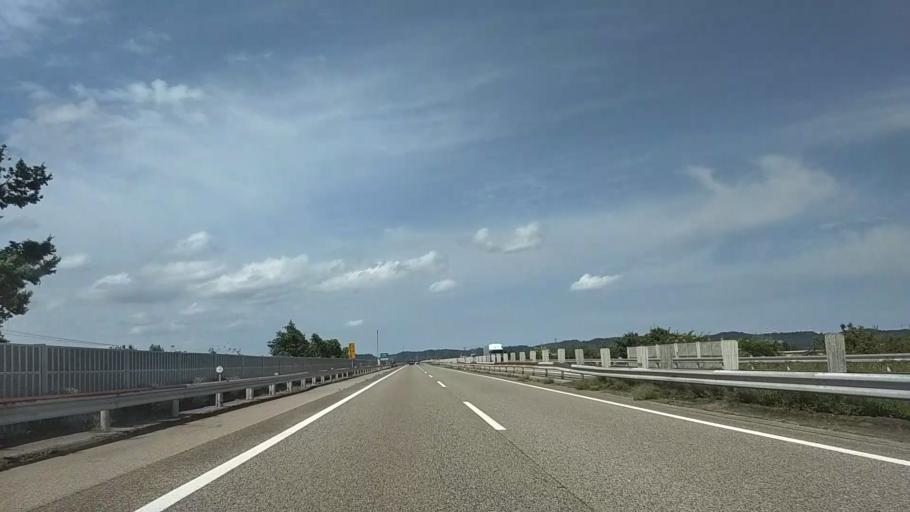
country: JP
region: Toyama
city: Toyama-shi
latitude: 36.6613
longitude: 137.1952
